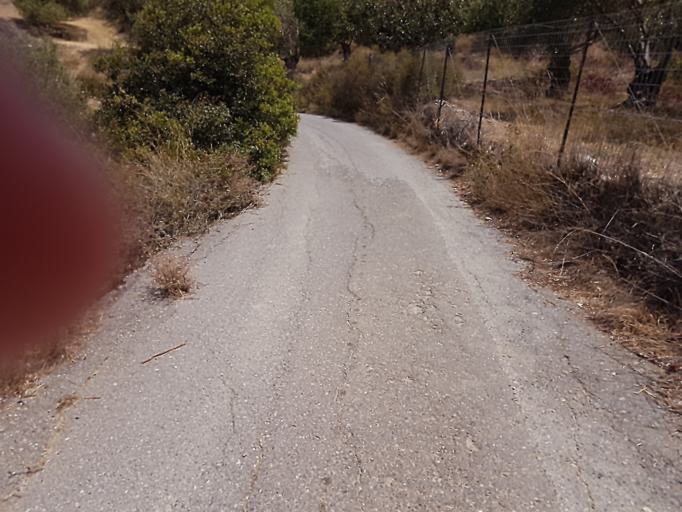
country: GR
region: Crete
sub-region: Nomos Irakleiou
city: Limin Khersonisou
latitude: 35.3107
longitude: 25.3815
